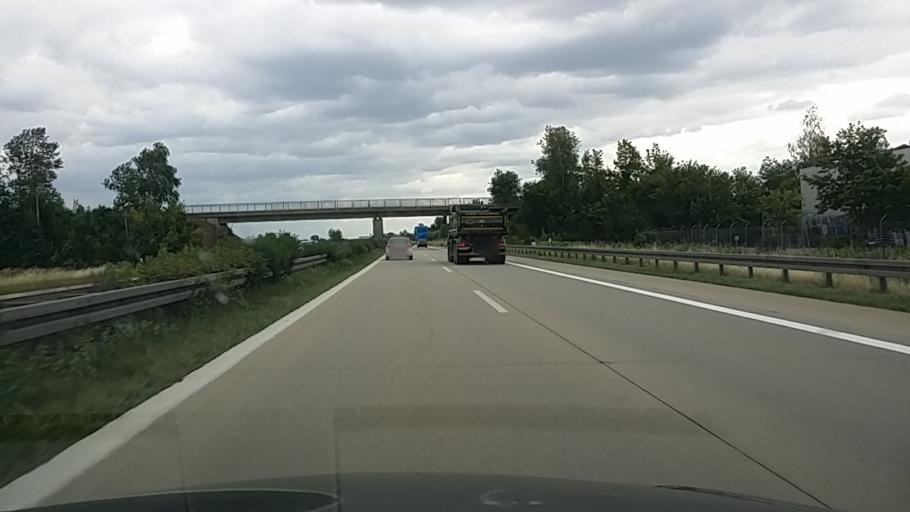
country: DE
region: Bavaria
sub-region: Lower Bavaria
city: Loiching
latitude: 48.6440
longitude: 12.4199
